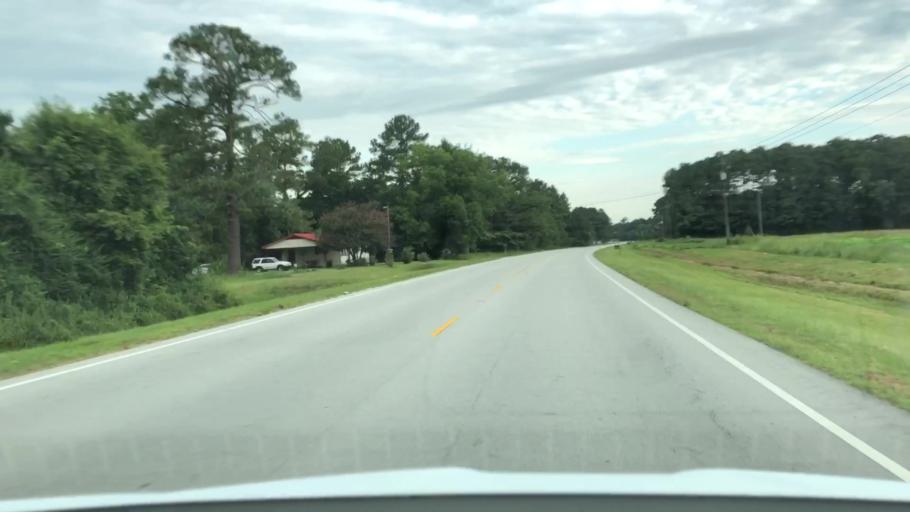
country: US
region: North Carolina
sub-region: Jones County
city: Trenton
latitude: 35.0208
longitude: -77.3038
